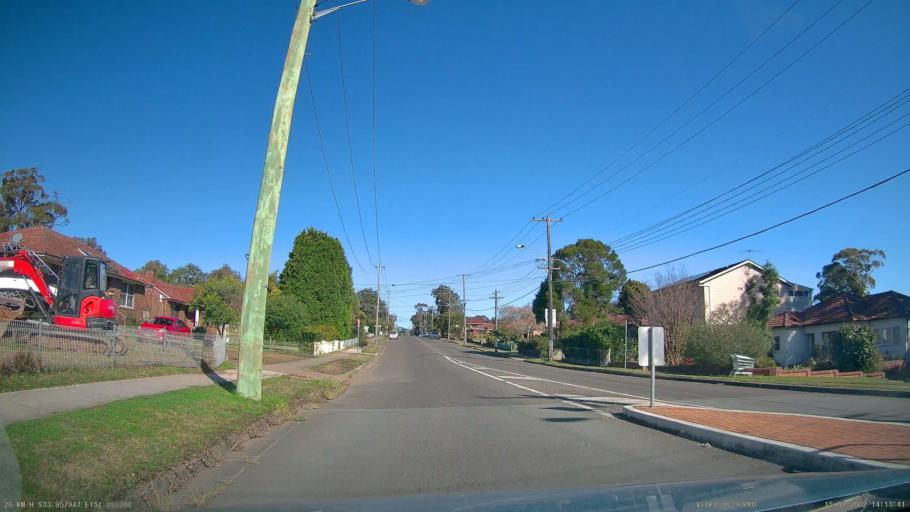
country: AU
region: New South Wales
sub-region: Hurstville
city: Peakhurst
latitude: -33.9580
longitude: 151.0512
